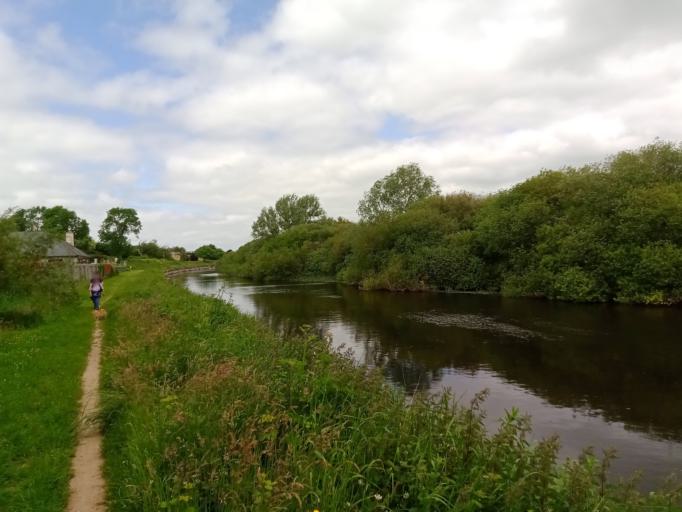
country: IE
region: Leinster
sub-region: County Carlow
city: Carlow
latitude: 52.8038
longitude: -6.9652
